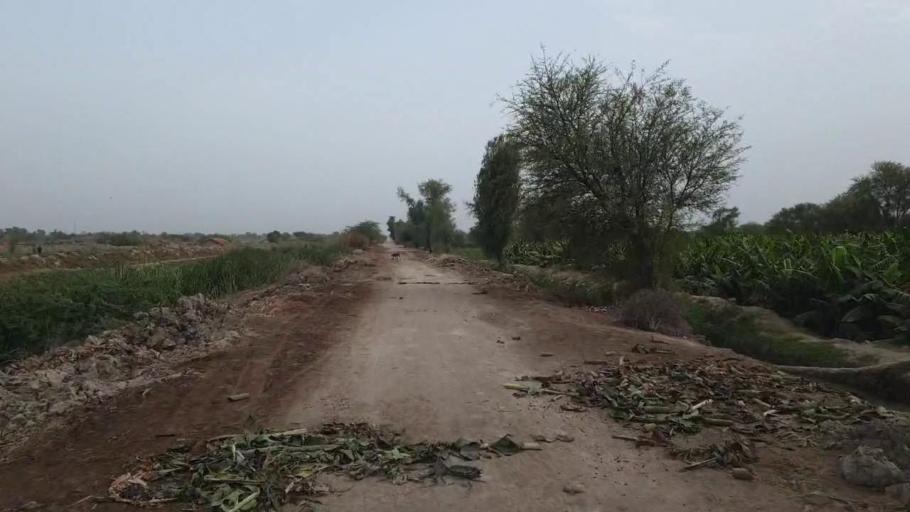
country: PK
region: Sindh
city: Daur
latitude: 26.4266
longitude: 68.2251
